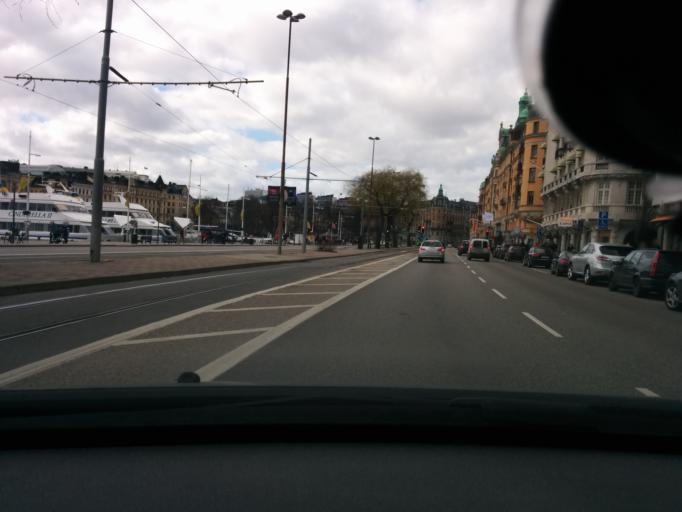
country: SE
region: Stockholm
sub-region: Stockholms Kommun
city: OEstermalm
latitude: 59.3318
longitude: 18.0809
